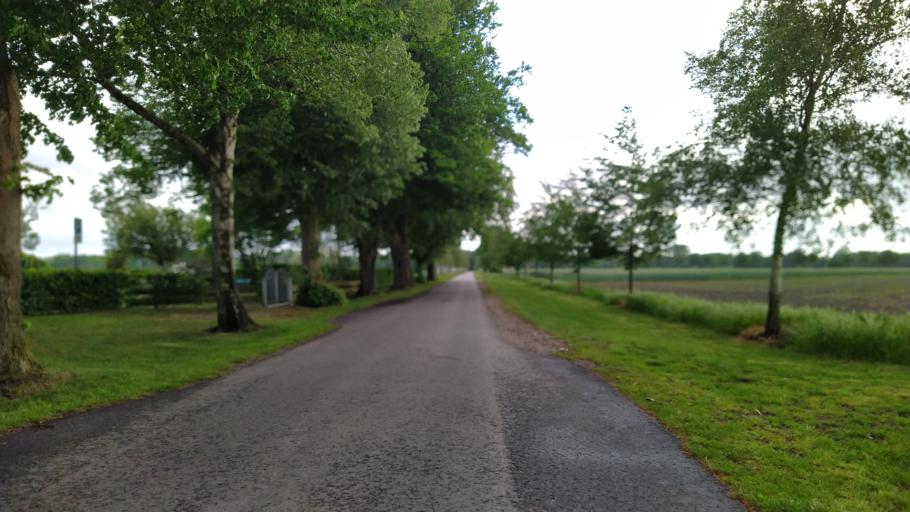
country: DE
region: Lower Saxony
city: Brest
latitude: 53.4394
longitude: 9.3605
